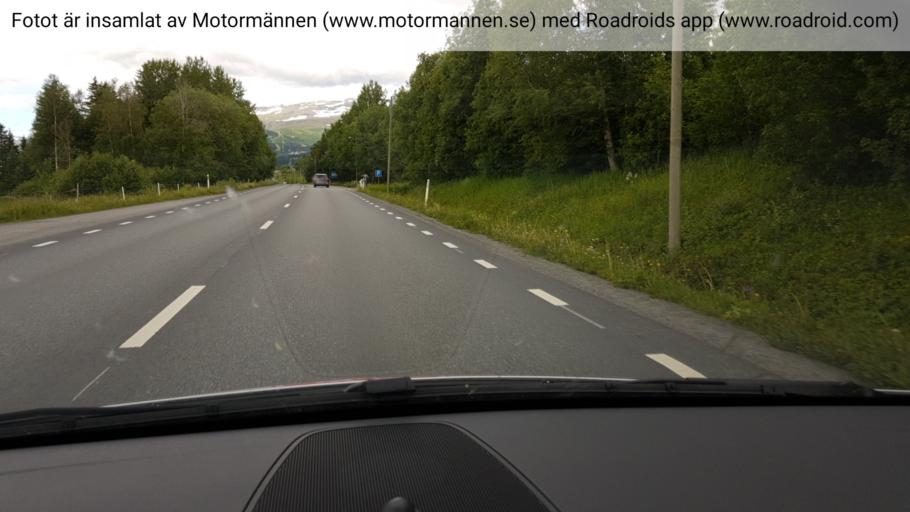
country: SE
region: Jaemtland
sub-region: Are Kommun
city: Are
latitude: 63.3584
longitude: 13.1813
